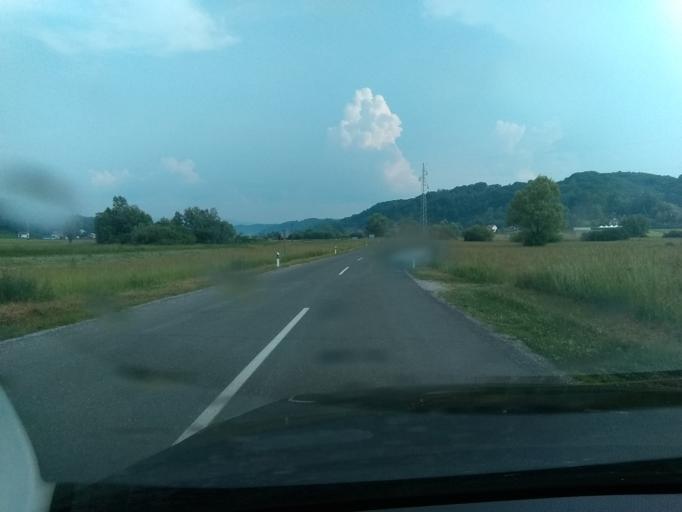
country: HR
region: Krapinsko-Zagorska
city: Pregrada
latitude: 46.0680
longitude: 15.7934
